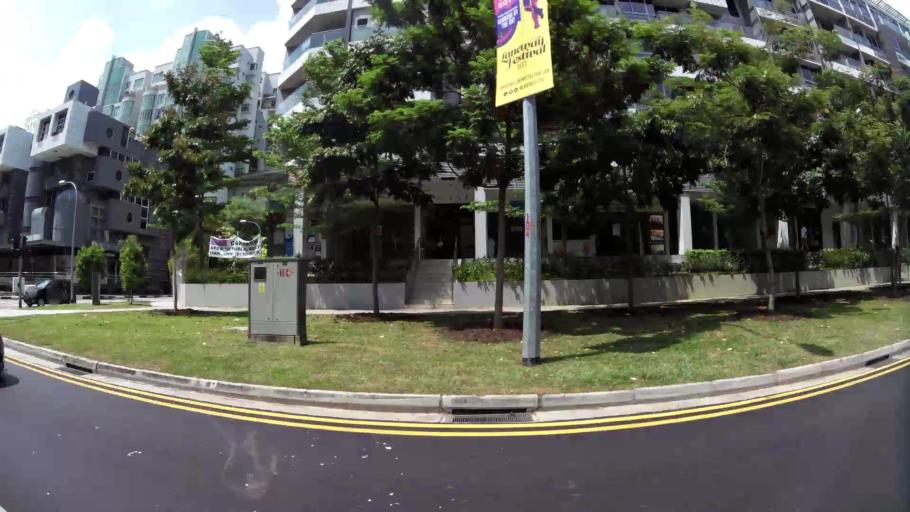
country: SG
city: Singapore
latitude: 1.2942
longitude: 103.8276
